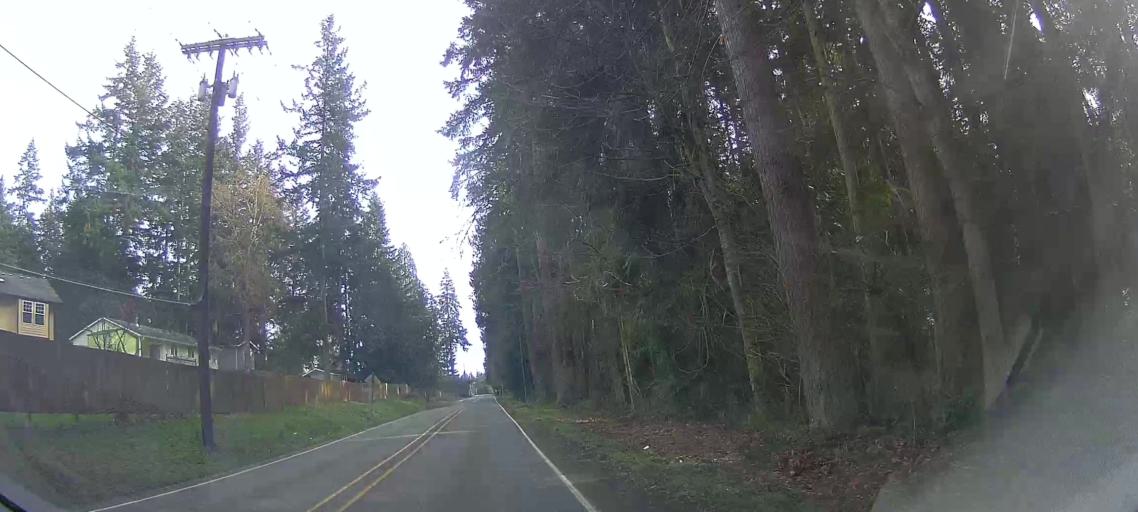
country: US
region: Washington
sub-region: Island County
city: Langley
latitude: 48.1086
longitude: -122.4286
